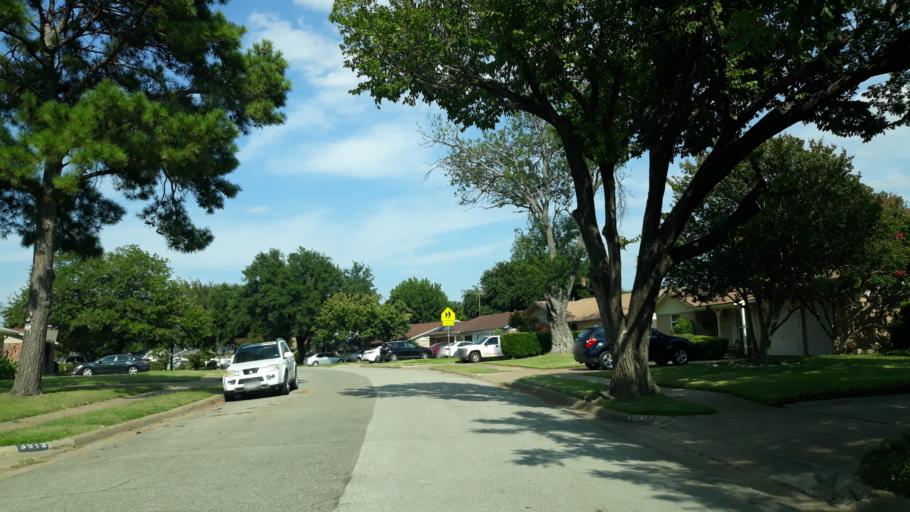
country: US
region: Texas
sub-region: Dallas County
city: Irving
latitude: 32.8410
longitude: -97.0043
